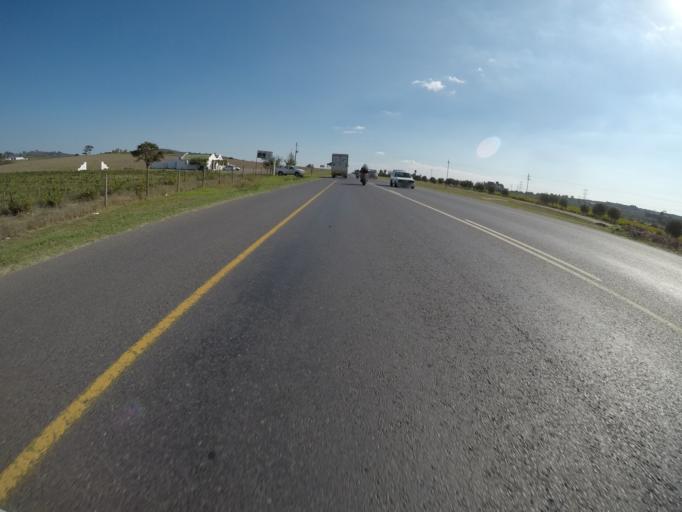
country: ZA
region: Western Cape
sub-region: City of Cape Town
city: Kraaifontein
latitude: -33.8905
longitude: 18.7417
